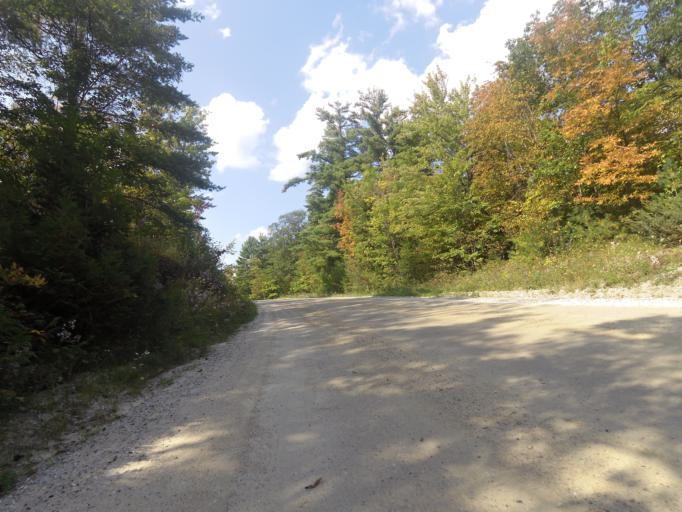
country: CA
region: Ontario
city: Renfrew
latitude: 45.1428
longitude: -76.6688
